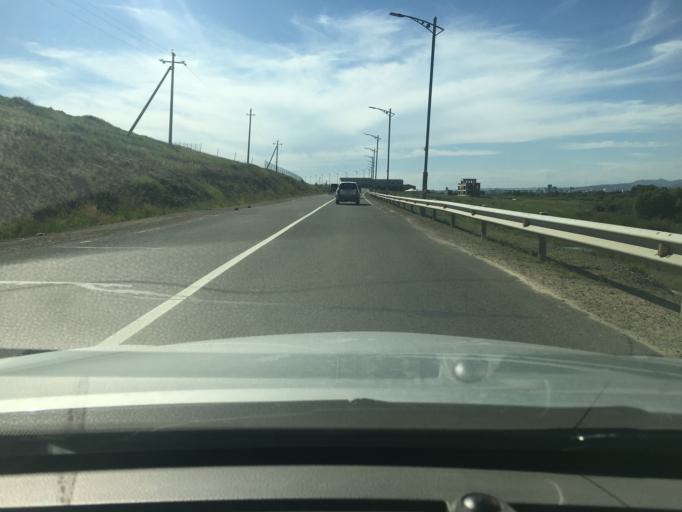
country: MN
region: Ulaanbaatar
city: Ulaanbaatar
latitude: 47.8860
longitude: 107.0110
